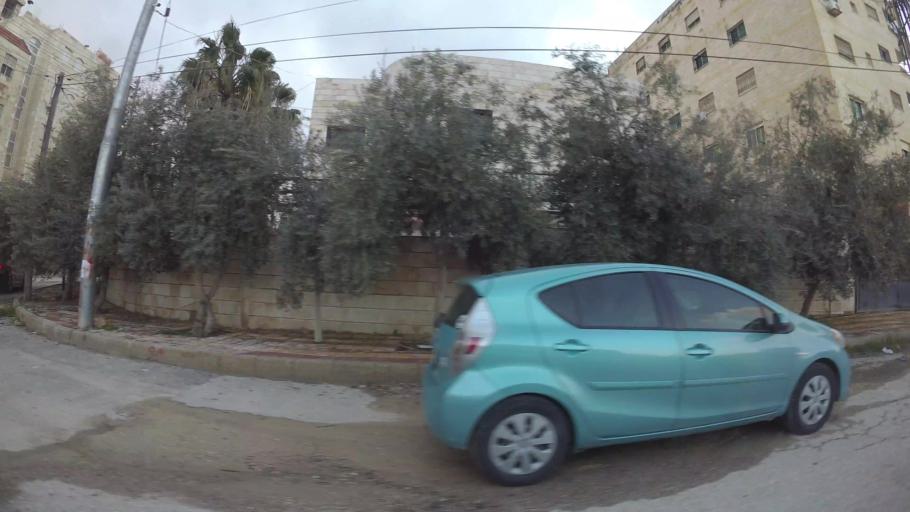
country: JO
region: Amman
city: Al Jubayhah
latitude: 32.0520
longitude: 35.8955
